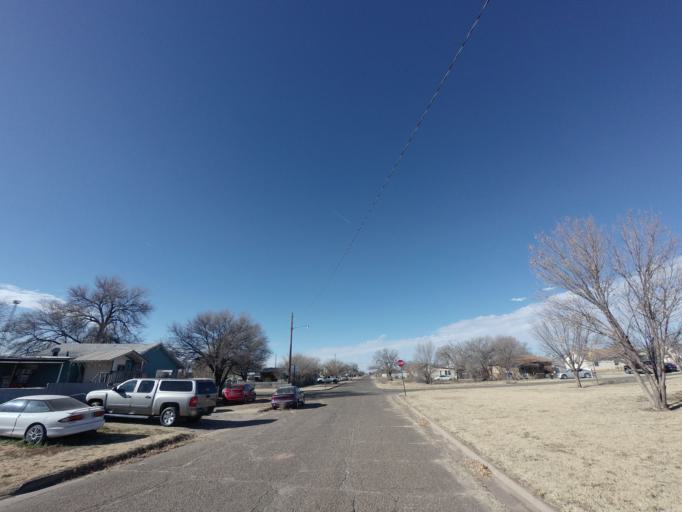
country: US
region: New Mexico
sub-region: Curry County
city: Clovis
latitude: 34.3997
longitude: -103.2113
